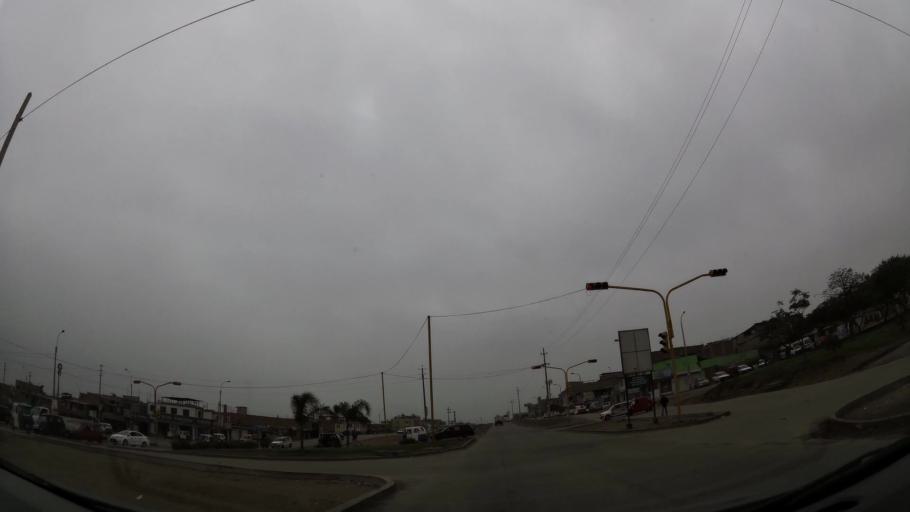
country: PE
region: Lima
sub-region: Lima
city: Surco
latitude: -12.2185
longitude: -76.9452
